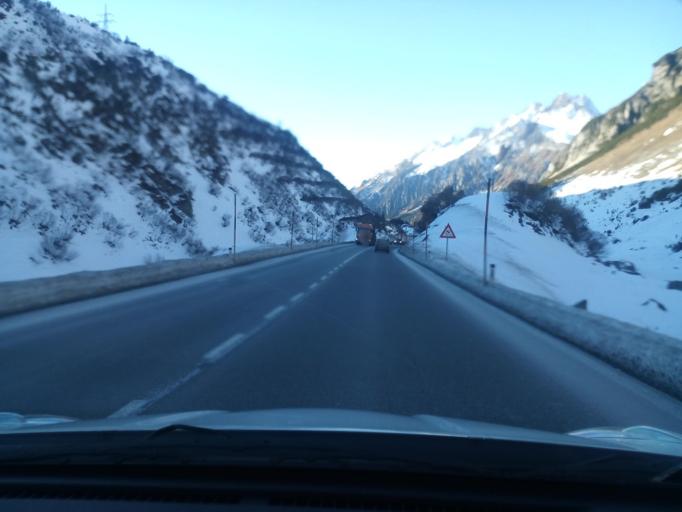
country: AT
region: Tyrol
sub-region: Politischer Bezirk Landeck
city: Sankt Anton am Arlberg
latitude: 47.1354
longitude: 10.2005
